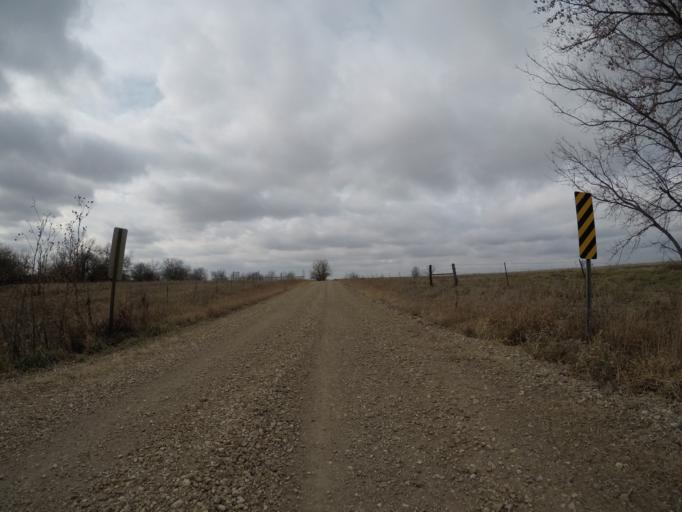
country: US
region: Kansas
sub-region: Morris County
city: Council Grove
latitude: 38.7244
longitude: -96.2121
